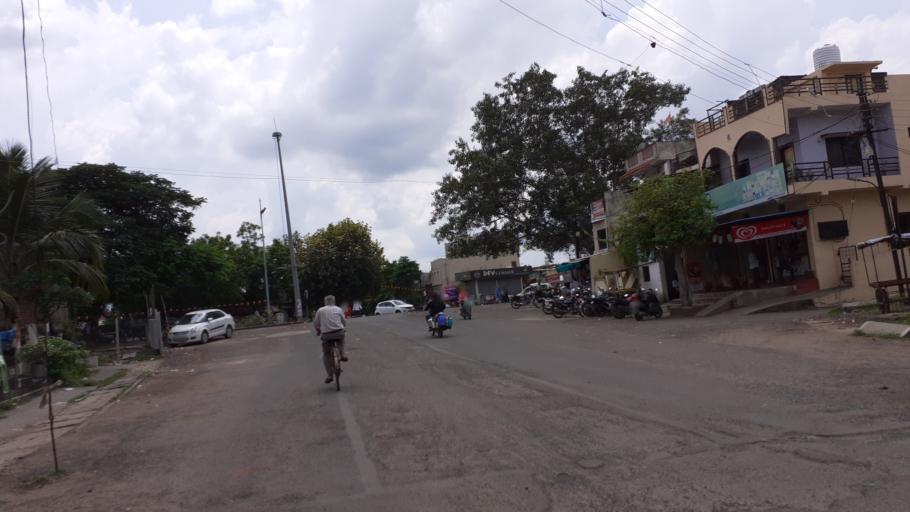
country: IN
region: Maharashtra
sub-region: Nagpur Division
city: Nagpur
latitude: 21.1076
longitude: 79.1170
